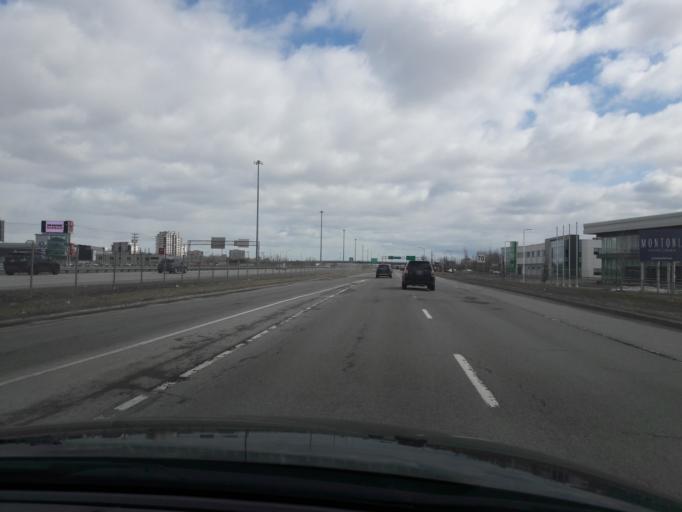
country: CA
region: Quebec
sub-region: Laurentides
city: Rosemere
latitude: 45.5615
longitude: -73.7841
